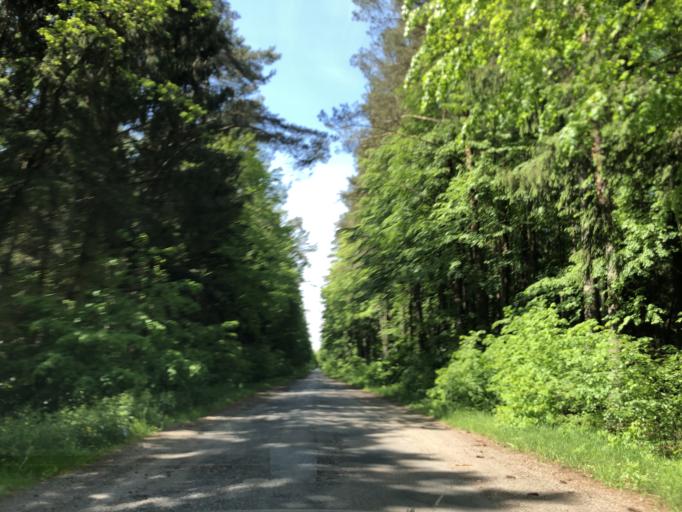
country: PL
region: West Pomeranian Voivodeship
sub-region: Powiat kolobrzeski
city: Dygowo
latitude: 54.0787
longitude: 15.7395
